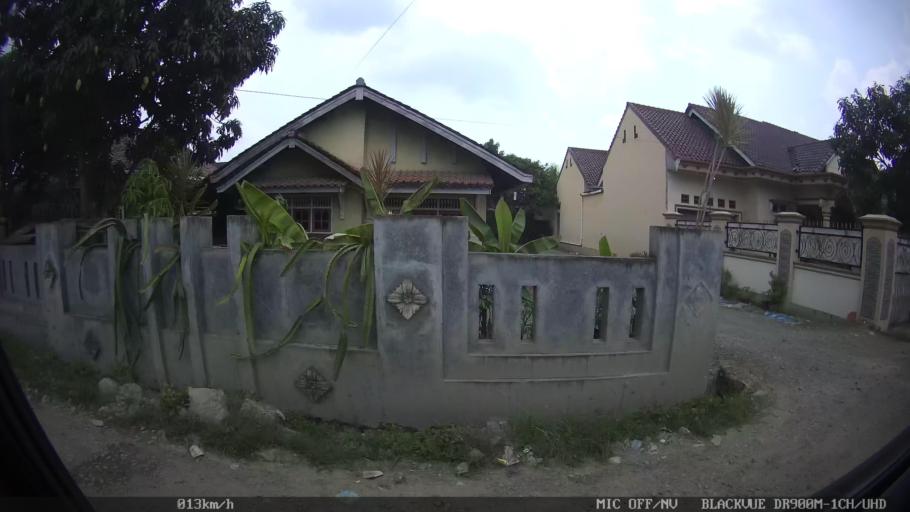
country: ID
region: Lampung
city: Gadingrejo
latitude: -5.3785
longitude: 105.0332
